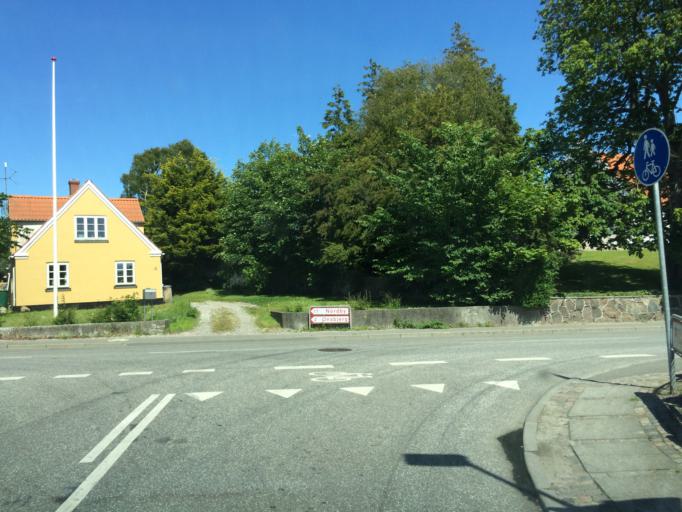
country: DK
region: Central Jutland
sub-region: Samso Kommune
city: Tranebjerg
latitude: 55.8342
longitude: 10.5855
